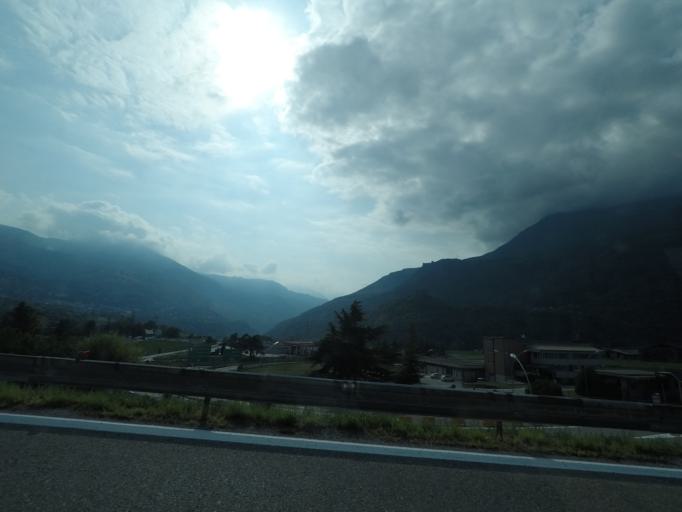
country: IT
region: Aosta Valley
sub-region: Valle d'Aosta
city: Chatillon
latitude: 45.7493
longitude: 7.6198
